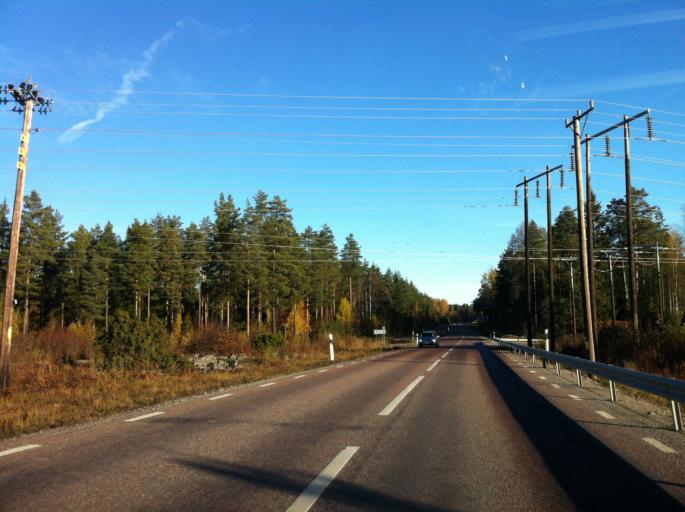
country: SE
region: Gaevleborg
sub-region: Gavle Kommun
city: Gavle
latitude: 60.6261
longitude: 17.1176
